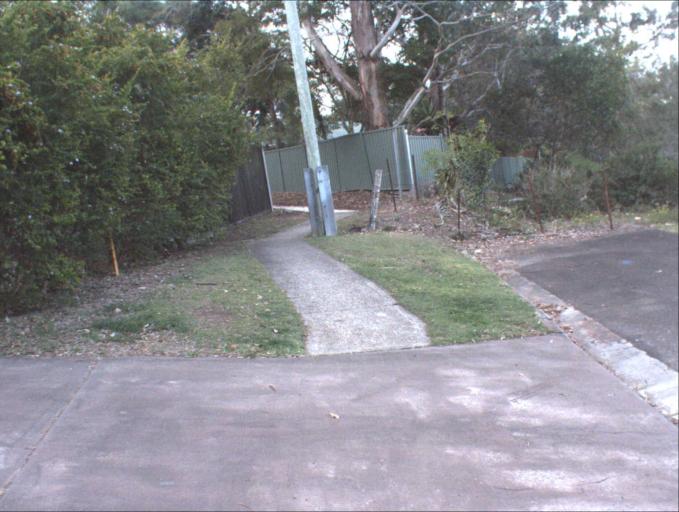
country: AU
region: Queensland
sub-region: Logan
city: Waterford West
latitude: -27.6801
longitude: 153.1347
